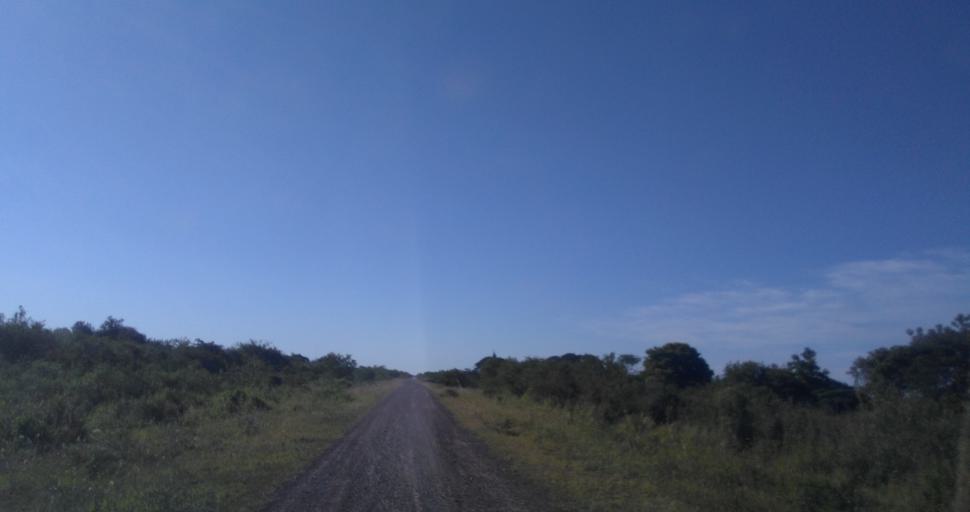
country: AR
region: Chaco
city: Barranqueras
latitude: -27.4273
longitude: -58.9269
